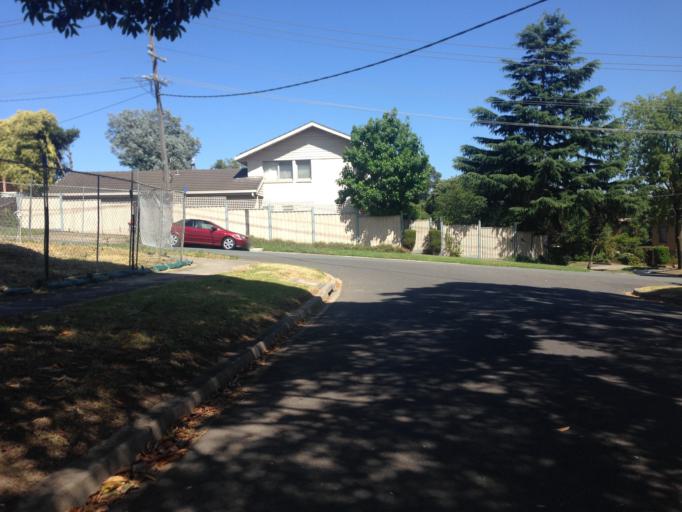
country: AU
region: Victoria
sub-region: Boroondara
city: Kew East
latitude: -37.7911
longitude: 145.0537
